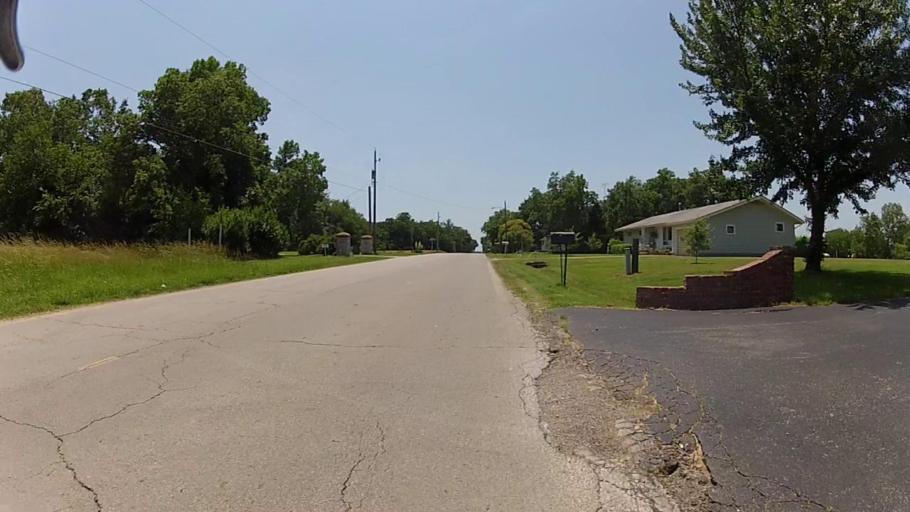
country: US
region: Kansas
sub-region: Montgomery County
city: Cherryvale
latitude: 37.2640
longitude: -95.5370
